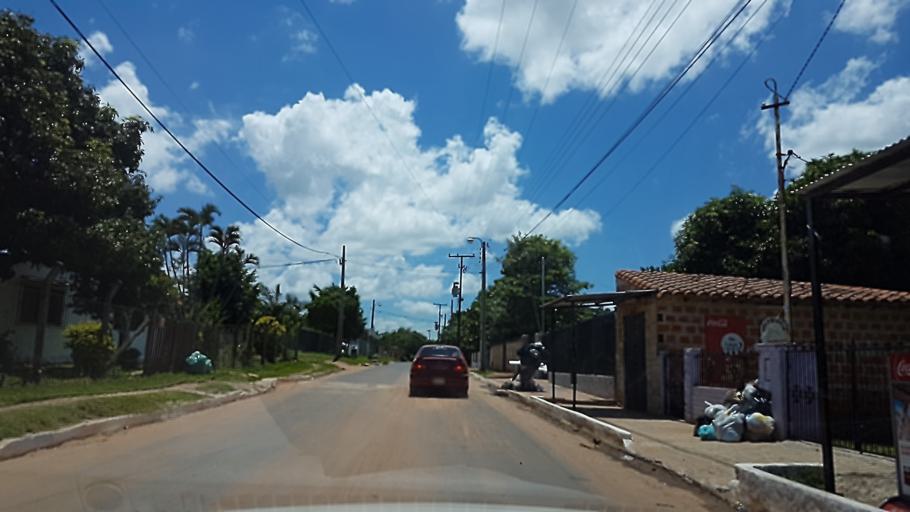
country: PY
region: Central
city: Colonia Mariano Roque Alonso
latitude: -25.2404
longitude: -57.5302
